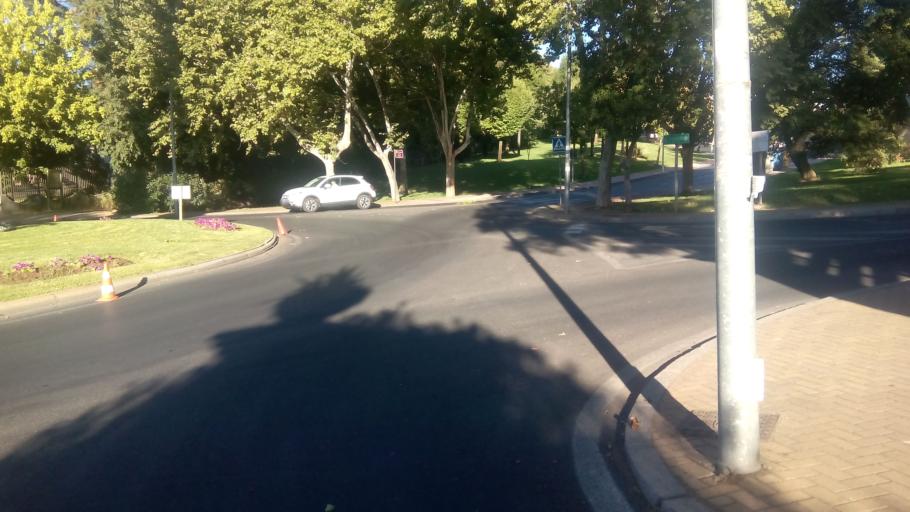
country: ES
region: Andalusia
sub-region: Province of Cordoba
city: Cordoba
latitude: 37.9070
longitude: -4.7985
